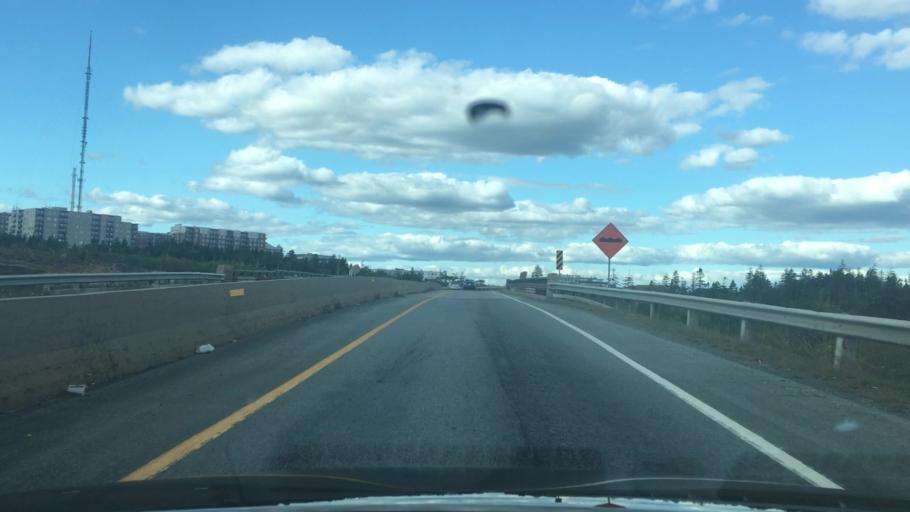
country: CA
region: Nova Scotia
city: Halifax
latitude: 44.6432
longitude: -63.6552
